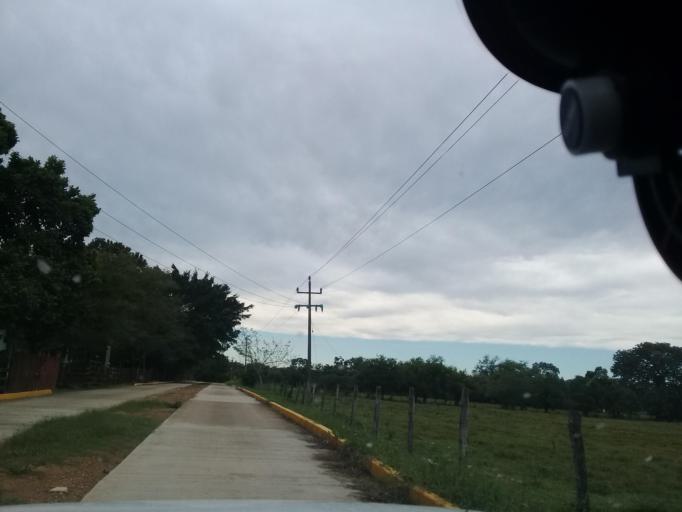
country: MX
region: Hidalgo
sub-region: Huejutla de Reyes
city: Chalahuiyapa
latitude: 21.1627
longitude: -98.3554
